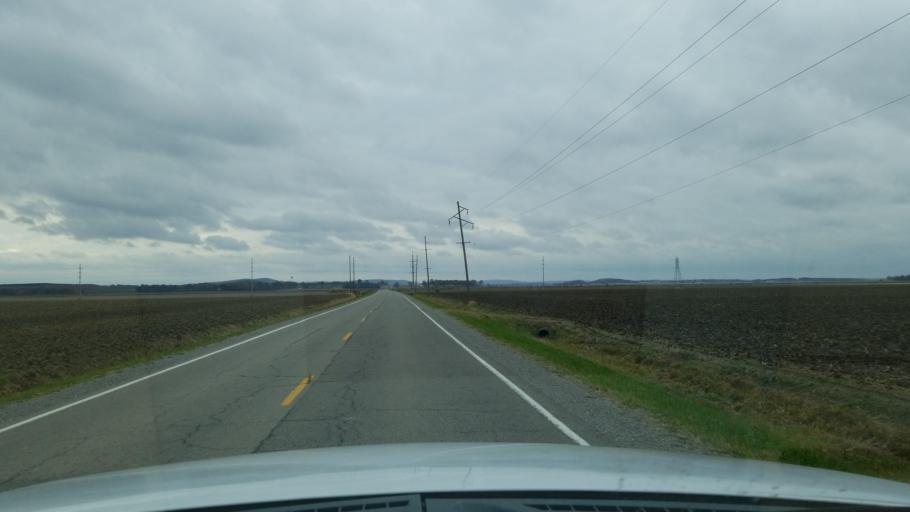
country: US
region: Illinois
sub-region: Saline County
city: Eldorado
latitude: 37.7788
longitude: -88.4383
